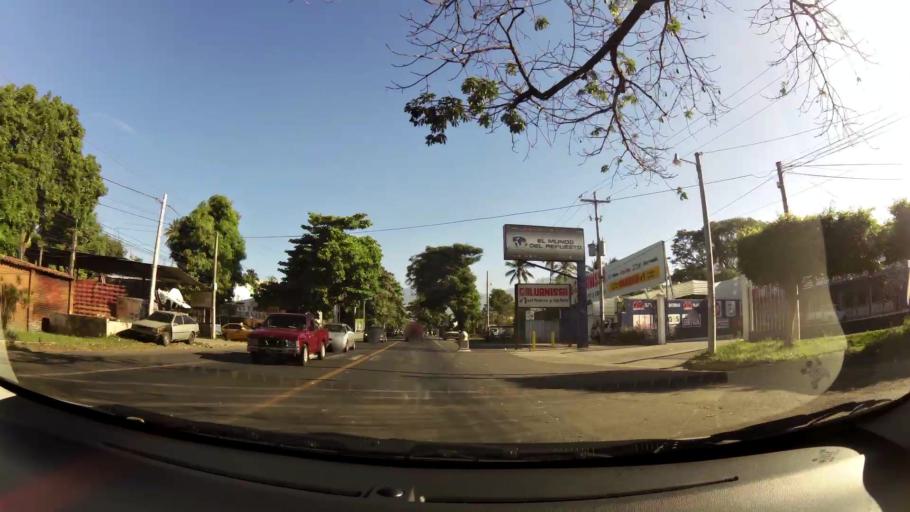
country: SV
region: Sonsonate
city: Sonzacate
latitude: 13.7286
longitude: -89.7154
